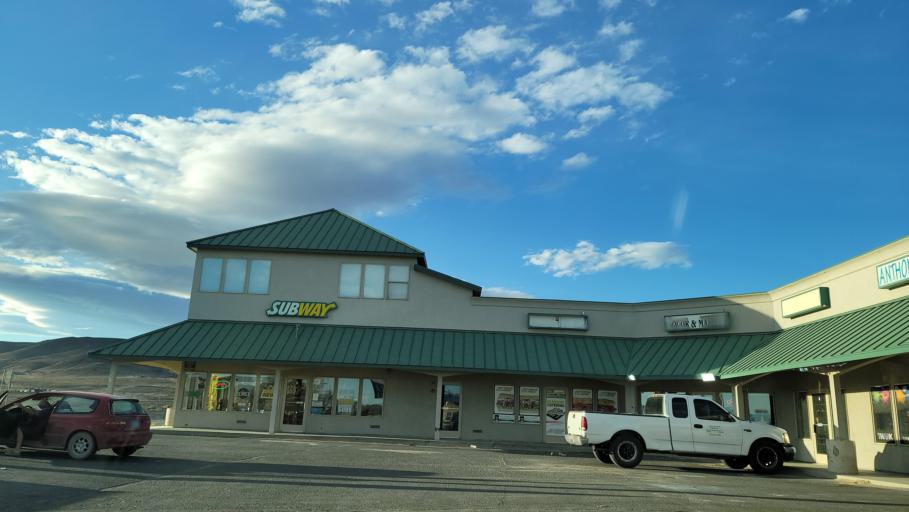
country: US
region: Nevada
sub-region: Lyon County
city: Silver Springs
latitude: 39.4077
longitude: -119.2263
